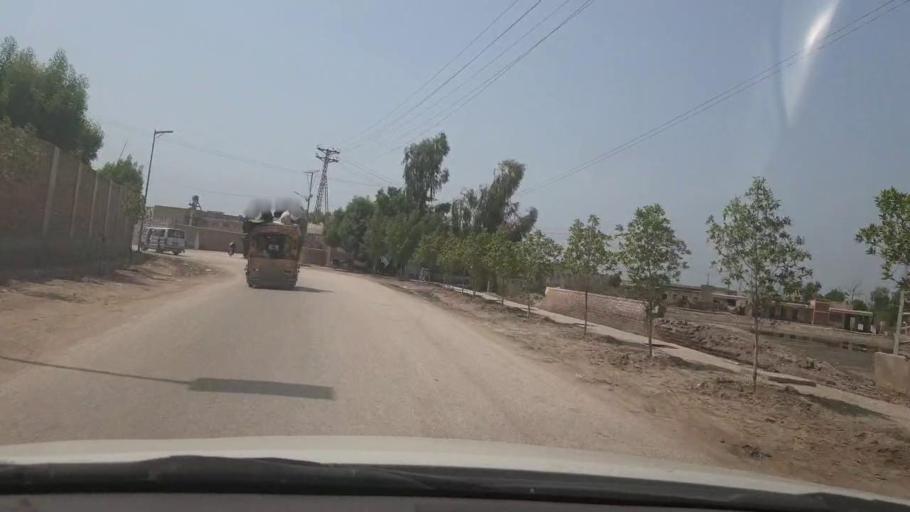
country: PK
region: Sindh
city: Garhi Yasin
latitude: 27.9104
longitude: 68.5120
